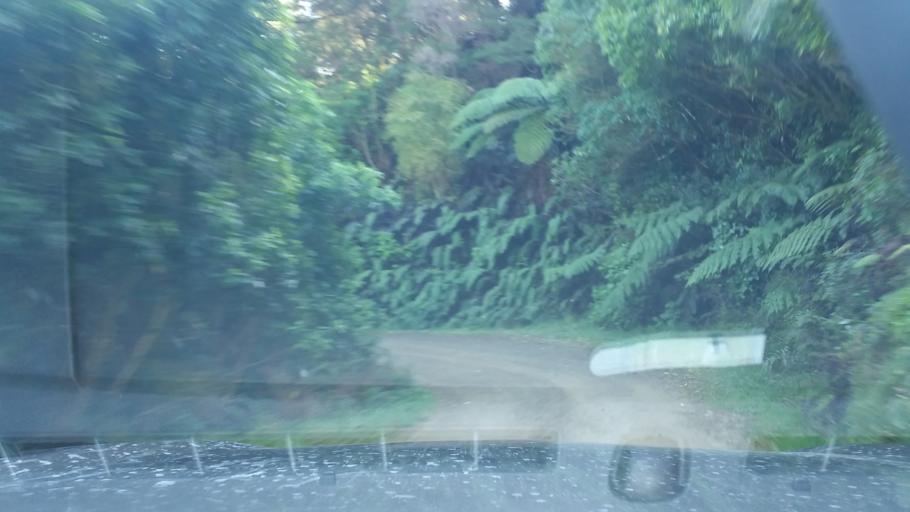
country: NZ
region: Marlborough
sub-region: Marlborough District
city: Picton
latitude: -41.1186
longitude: 173.9951
